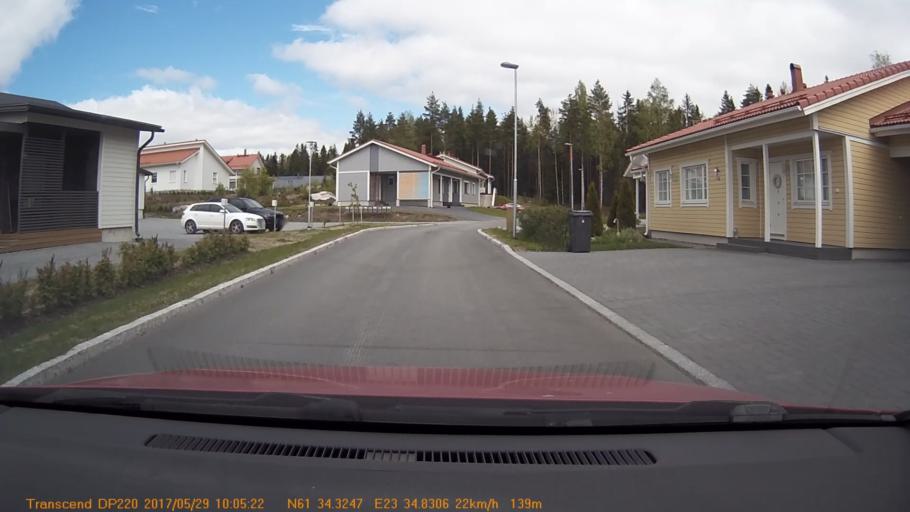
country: FI
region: Pirkanmaa
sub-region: Tampere
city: Yloejaervi
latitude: 61.5721
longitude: 23.5805
